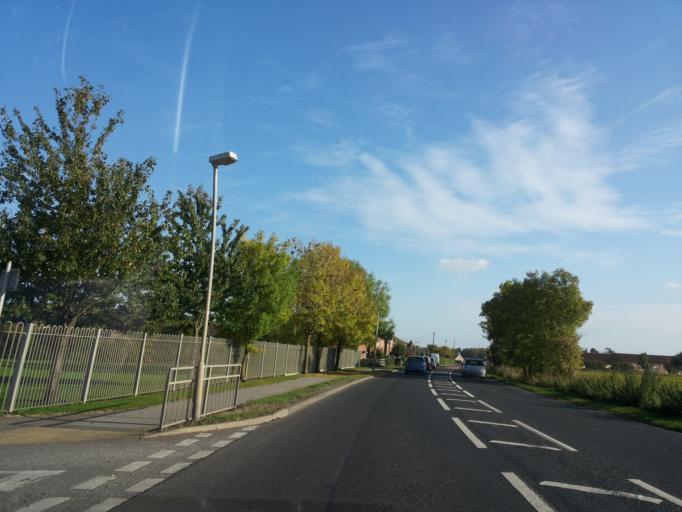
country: GB
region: England
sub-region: East Riding of Yorkshire
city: Snaith
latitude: 53.6861
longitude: -0.9987
